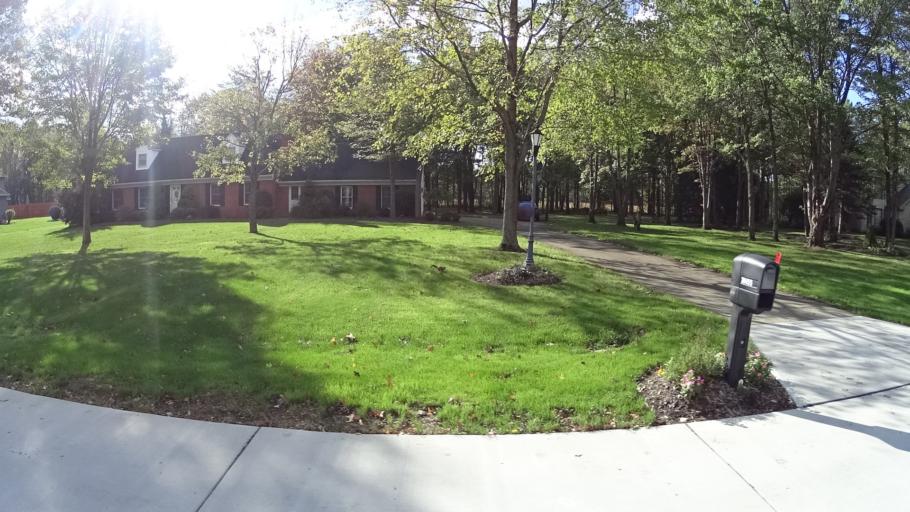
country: US
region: Ohio
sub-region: Lorain County
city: Grafton
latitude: 41.2962
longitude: -82.0722
